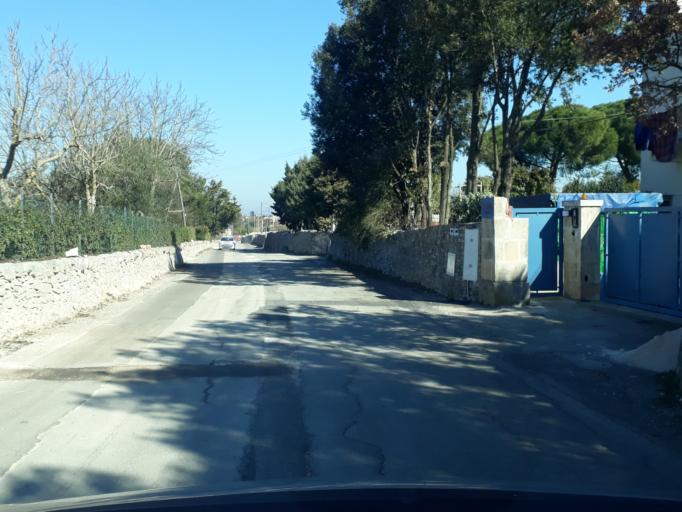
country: IT
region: Apulia
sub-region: Provincia di Taranto
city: Martina Franca
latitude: 40.7130
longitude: 17.3424
